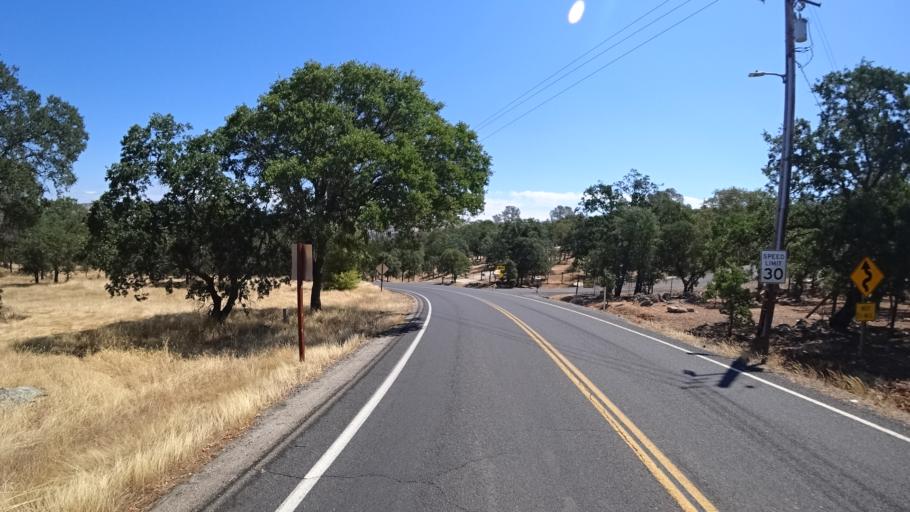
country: US
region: California
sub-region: Calaveras County
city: Copperopolis
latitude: 37.9352
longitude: -120.6370
